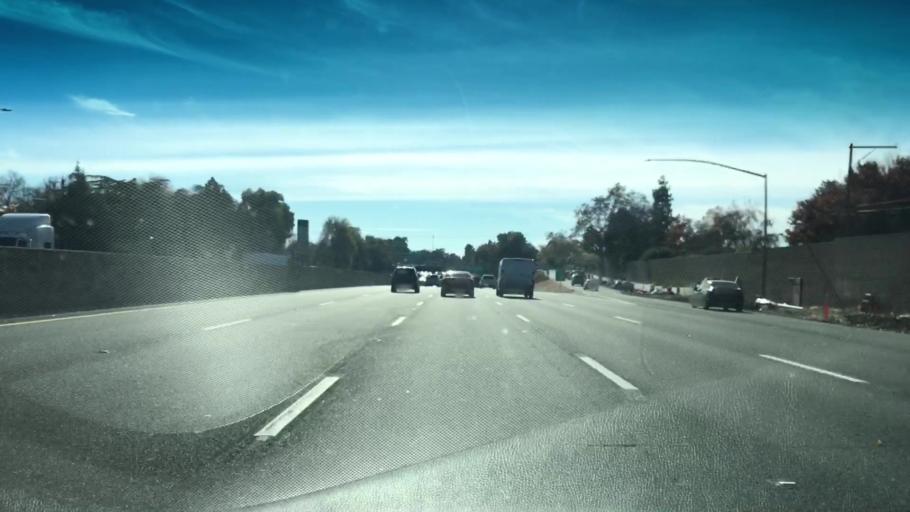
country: US
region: California
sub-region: Sacramento County
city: Sacramento
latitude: 38.5443
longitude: -121.4740
